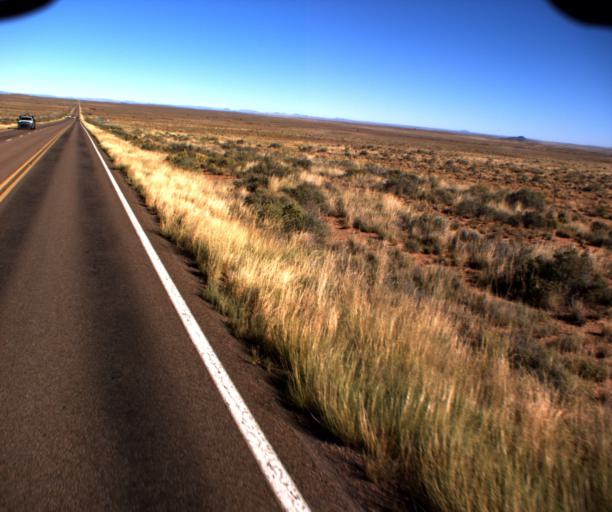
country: US
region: Arizona
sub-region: Navajo County
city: Snowflake
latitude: 34.6956
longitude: -110.1074
